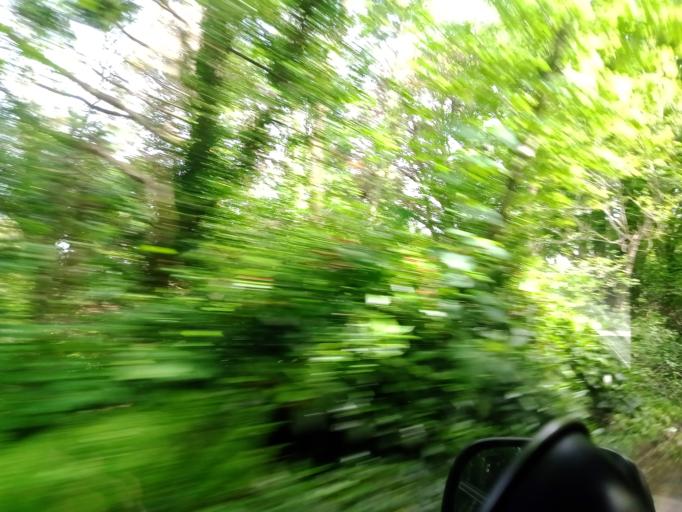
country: IE
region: Munster
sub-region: County Cork
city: Skibbereen
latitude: 51.5184
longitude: -9.3388
